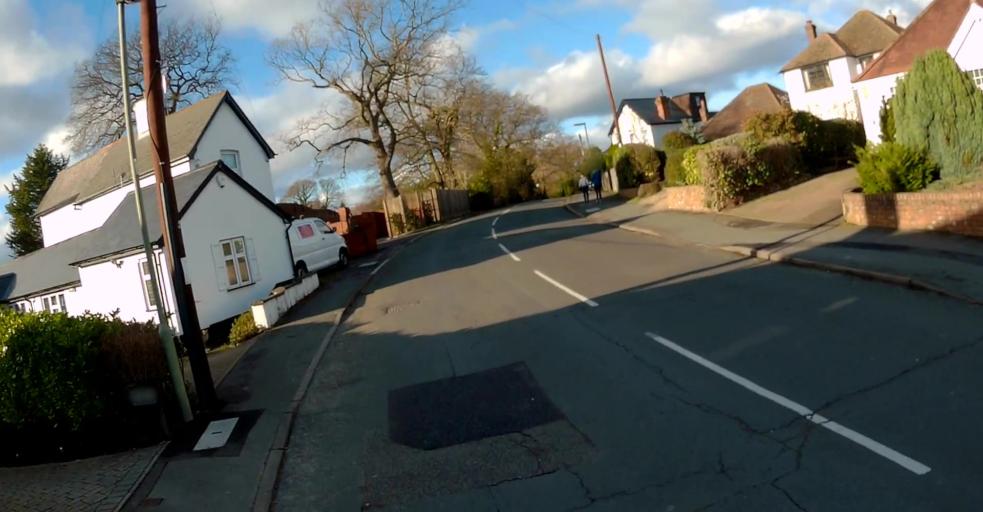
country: GB
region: England
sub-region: Surrey
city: Ottershaw
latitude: 51.3633
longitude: -0.5131
